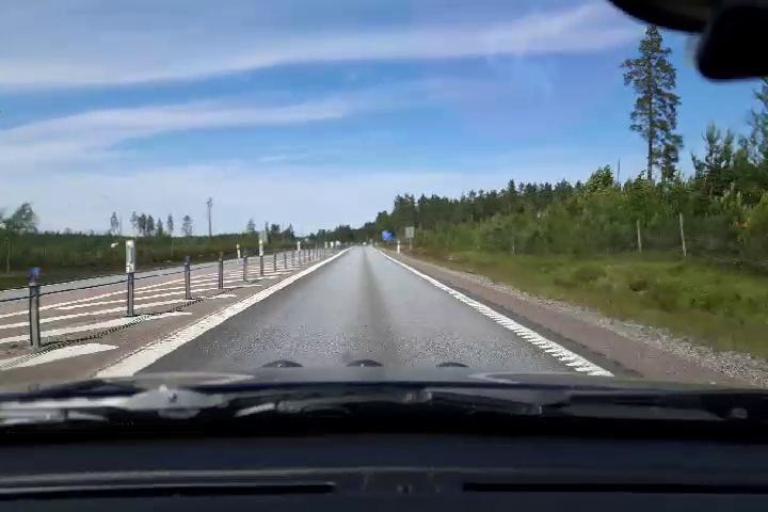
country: SE
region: Gaevleborg
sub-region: Gavle Kommun
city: Norrsundet
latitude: 61.0605
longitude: 16.9623
